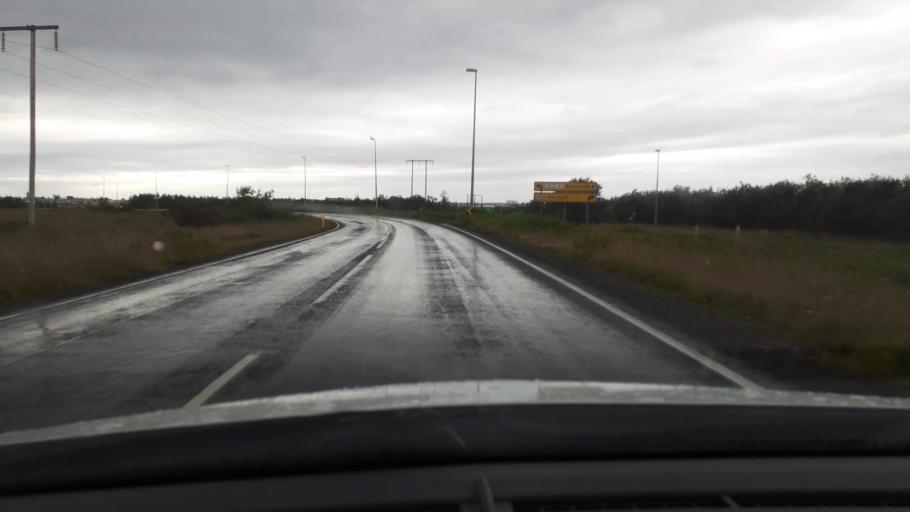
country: IS
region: West
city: Akranes
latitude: 64.3315
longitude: -22.0365
